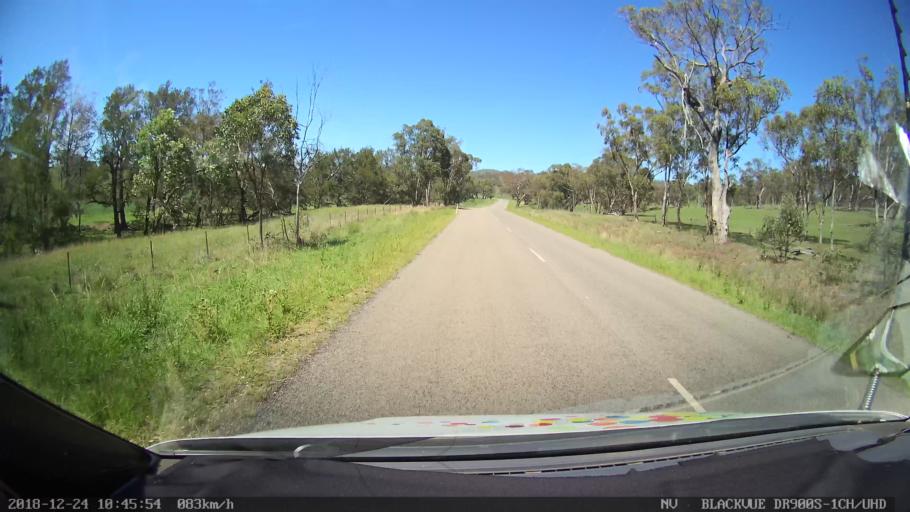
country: AU
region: New South Wales
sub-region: Upper Hunter Shire
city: Merriwa
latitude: -31.9071
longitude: 150.4324
